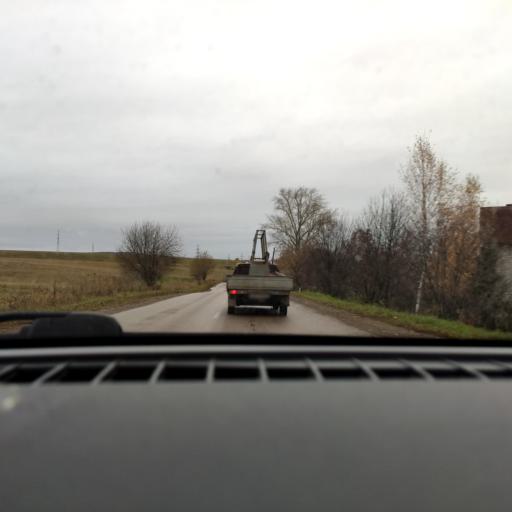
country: RU
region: Perm
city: Ferma
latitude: 57.9209
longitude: 56.3276
